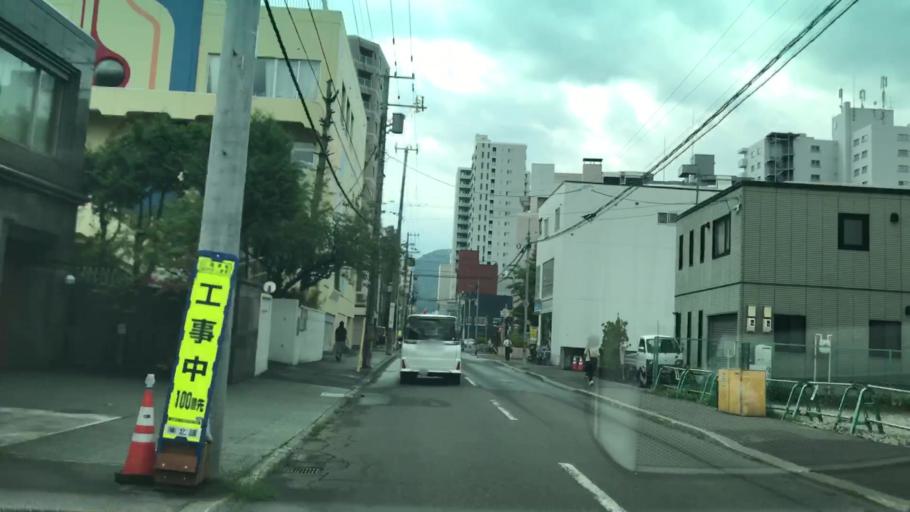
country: JP
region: Hokkaido
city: Sapporo
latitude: 43.0596
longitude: 141.3210
